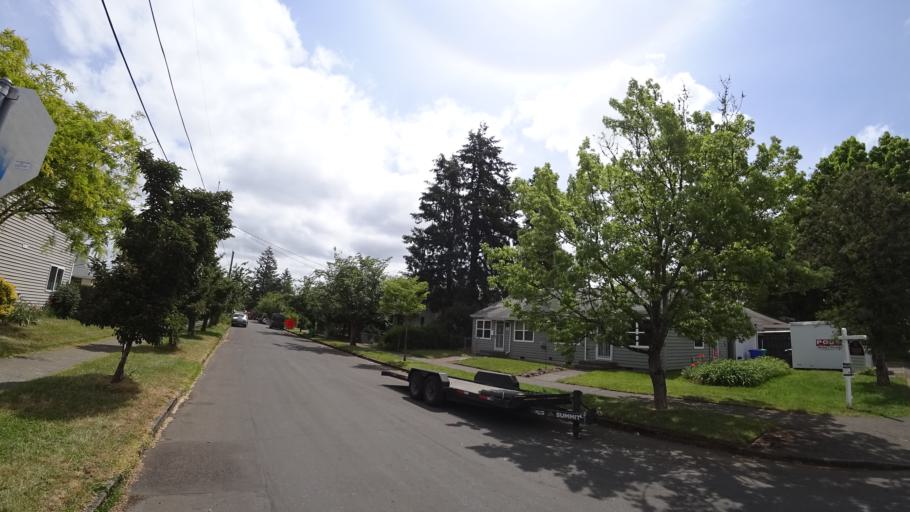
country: US
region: Oregon
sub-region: Multnomah County
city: Lents
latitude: 45.4810
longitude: -122.5970
